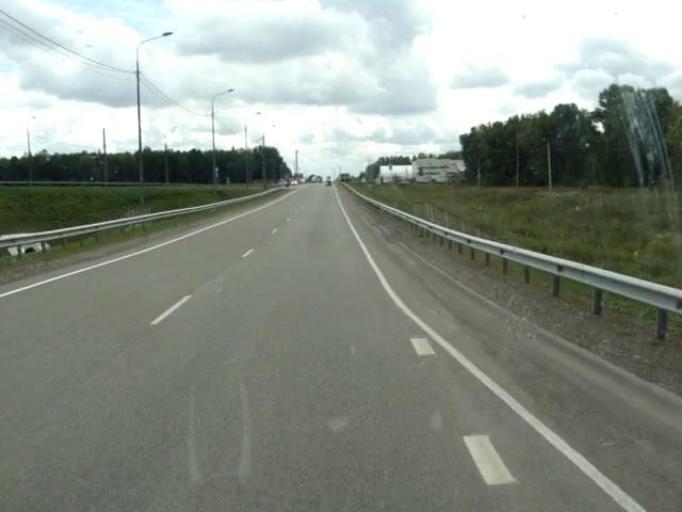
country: RU
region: Altai Krai
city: Zarya
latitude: 52.5780
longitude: 85.1780
